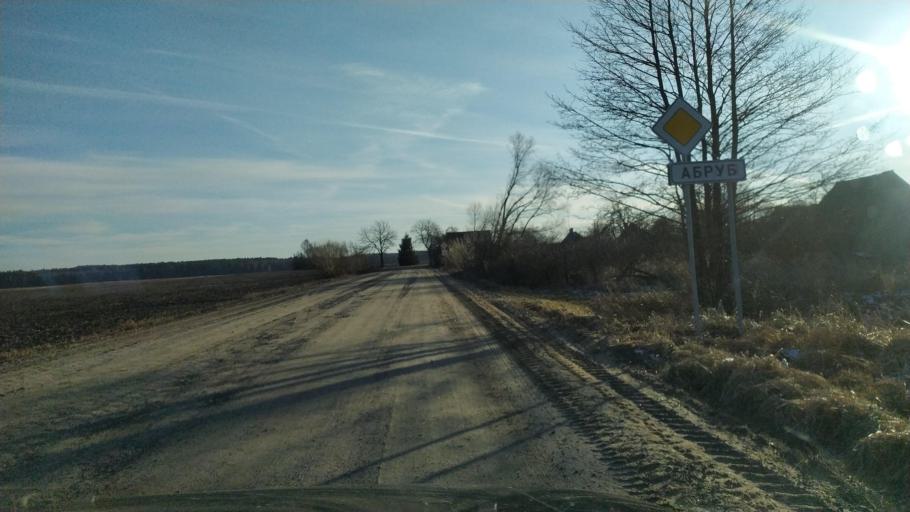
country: BY
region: Brest
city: Pruzhany
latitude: 52.5521
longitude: 24.2950
